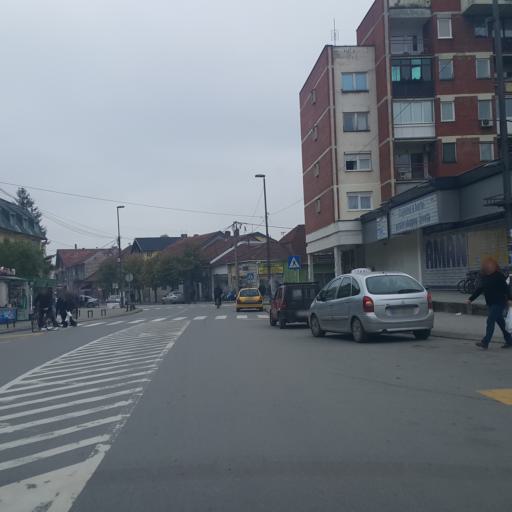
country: RS
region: Central Serbia
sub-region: Zajecarski Okrug
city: Zajecar
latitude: 43.9035
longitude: 22.2810
